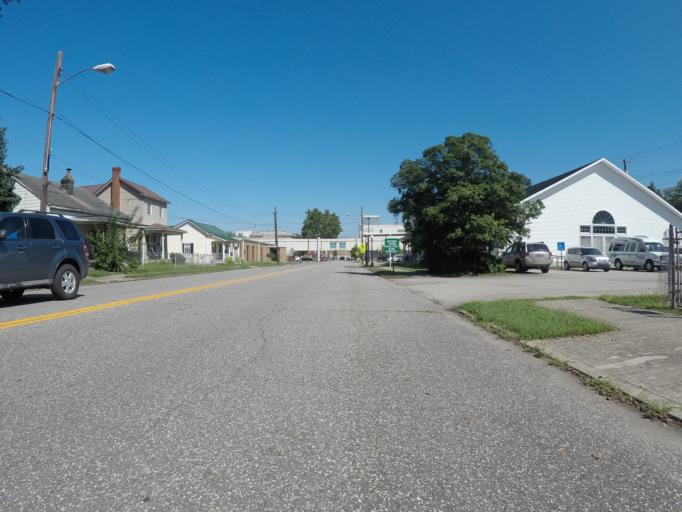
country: US
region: Kentucky
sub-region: Boyd County
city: Catlettsburg
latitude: 38.4137
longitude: -82.5983
